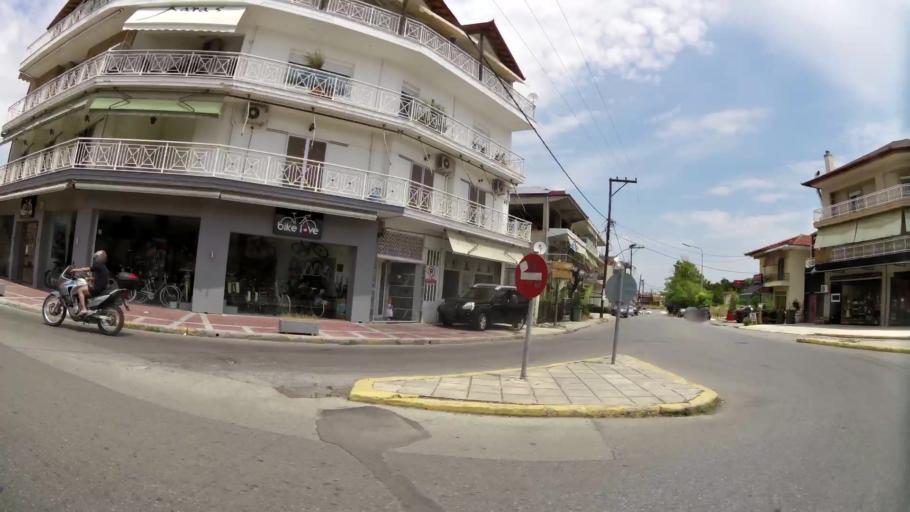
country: GR
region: Central Macedonia
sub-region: Nomos Pierias
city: Katerini
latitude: 40.2677
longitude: 22.5225
